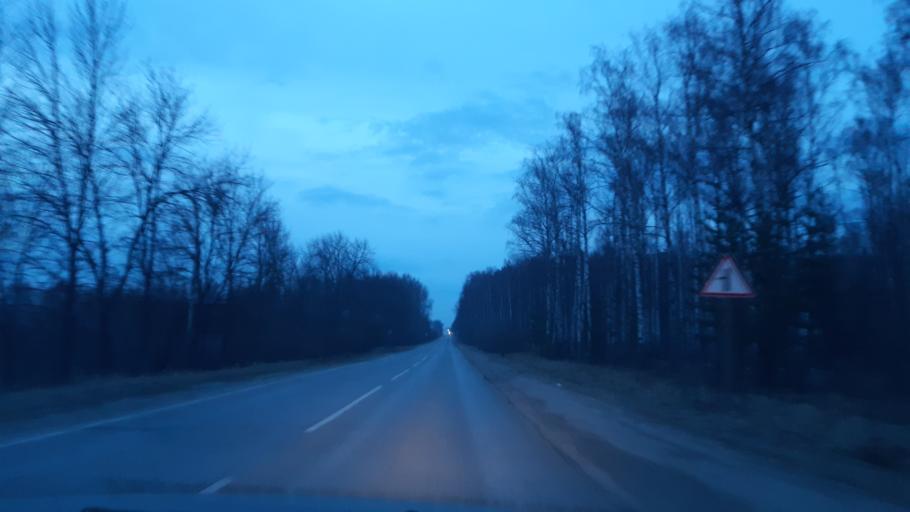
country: RU
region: Vladimir
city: Luknovo
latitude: 56.2248
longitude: 42.0349
